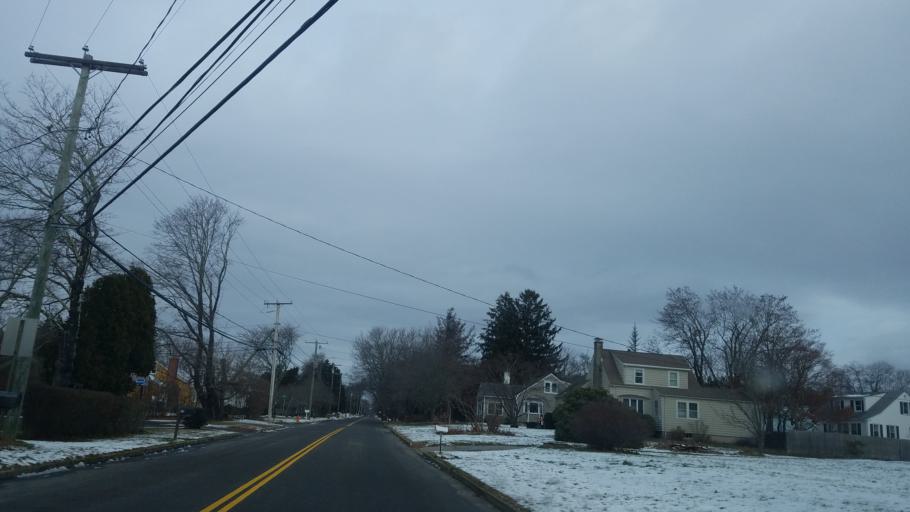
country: US
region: Connecticut
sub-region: New London County
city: Central Waterford
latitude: 41.3379
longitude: -72.1540
